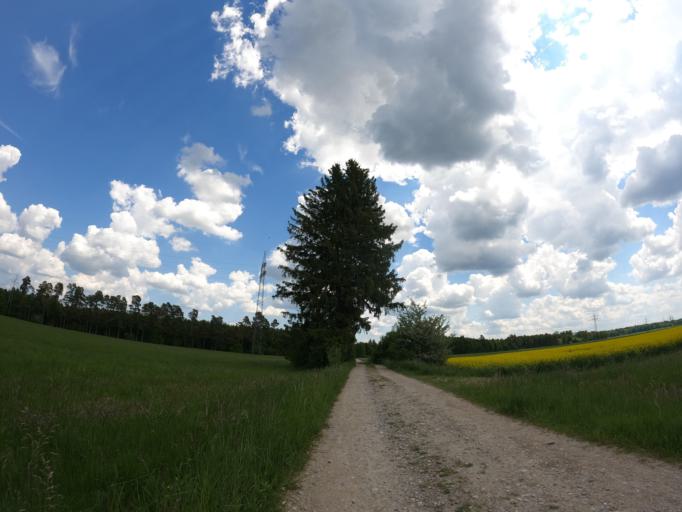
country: DE
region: Bavaria
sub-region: Upper Bavaria
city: Sauerlach
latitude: 47.9840
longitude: 11.6669
